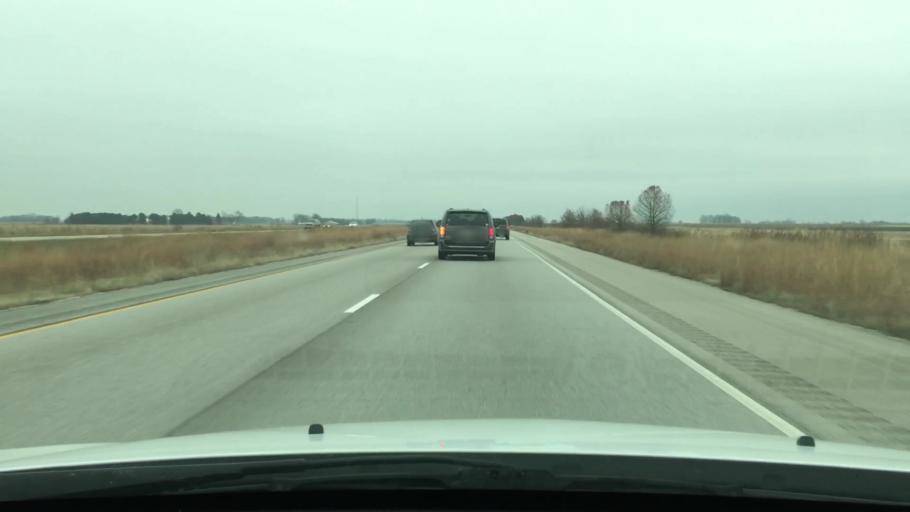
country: US
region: Illinois
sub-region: Sangamon County
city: New Berlin
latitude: 39.7369
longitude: -90.0125
